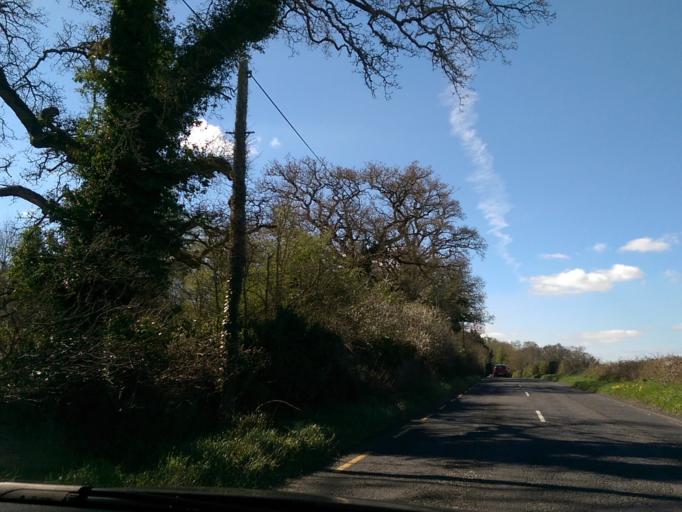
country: IE
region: Leinster
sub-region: Laois
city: Stradbally
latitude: 53.0172
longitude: -7.0923
